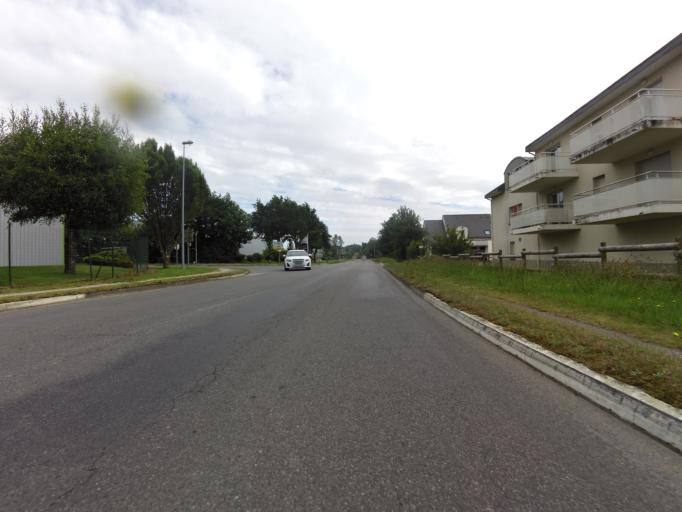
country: FR
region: Brittany
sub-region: Departement du Morbihan
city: Questembert
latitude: 47.6658
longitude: -2.4412
